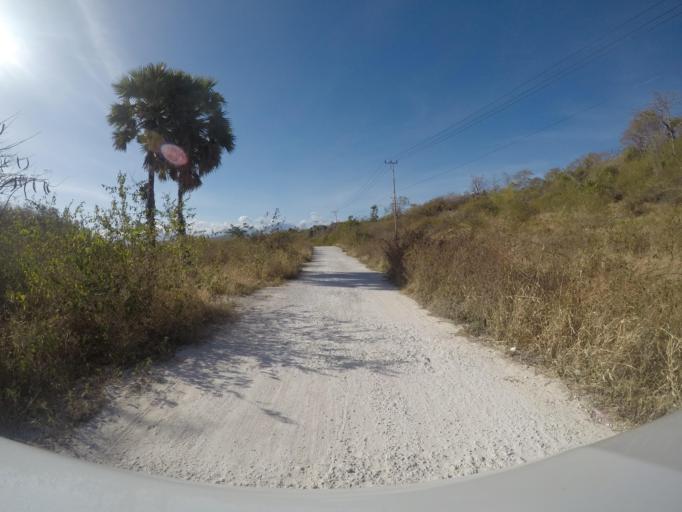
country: TL
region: Baucau
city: Baucau
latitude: -8.4484
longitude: 126.4270
